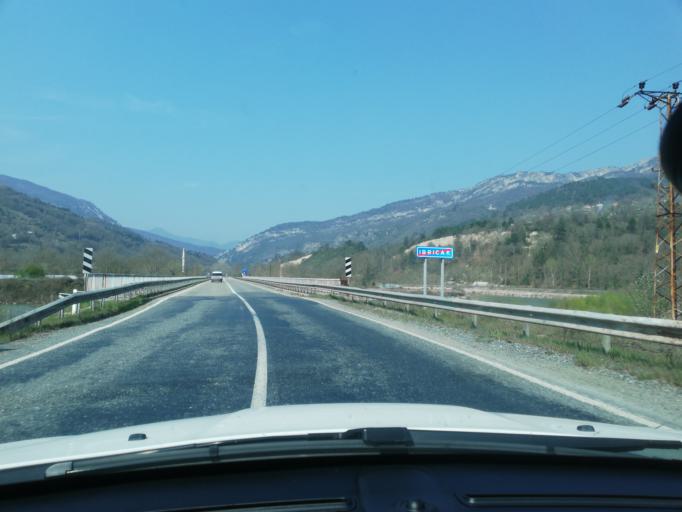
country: TR
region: Karabuk
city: Yenice
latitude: 41.2160
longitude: 32.2619
